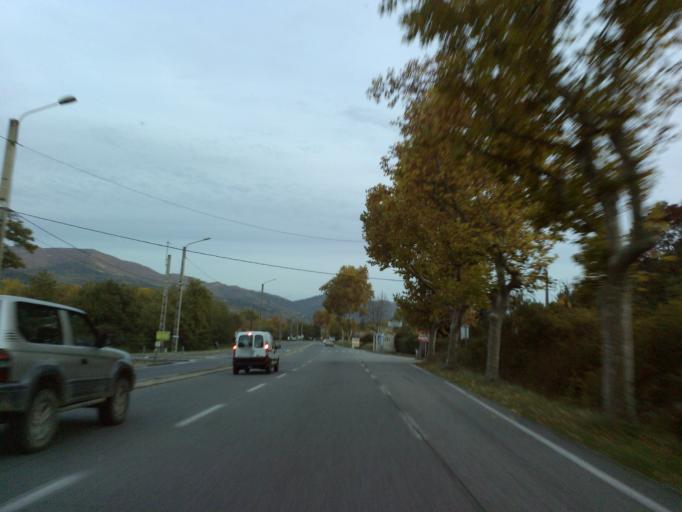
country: FR
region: Provence-Alpes-Cote d'Azur
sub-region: Departement des Alpes-de-Haute-Provence
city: Volonne
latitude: 44.1071
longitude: 6.0043
